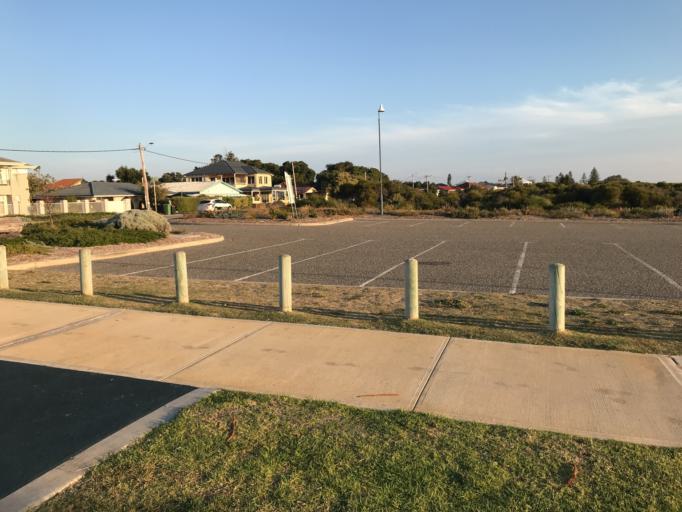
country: AU
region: Western Australia
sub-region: Rockingham
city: Shoalwater
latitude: -32.3002
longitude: 115.7040
